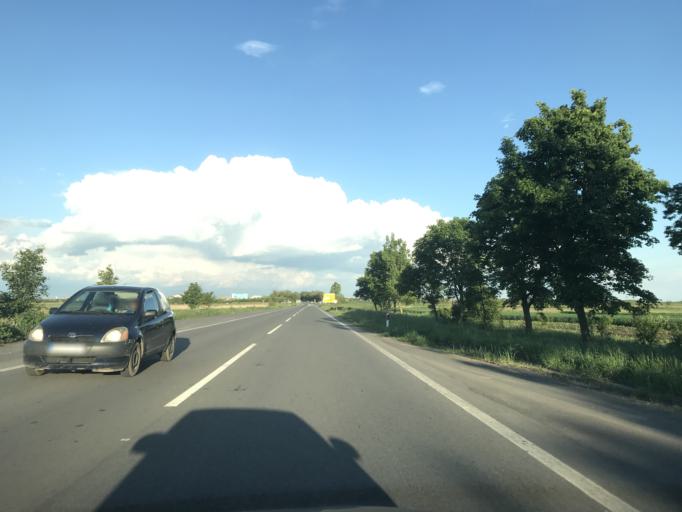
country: RS
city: Aradac
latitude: 45.3827
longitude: 20.3316
